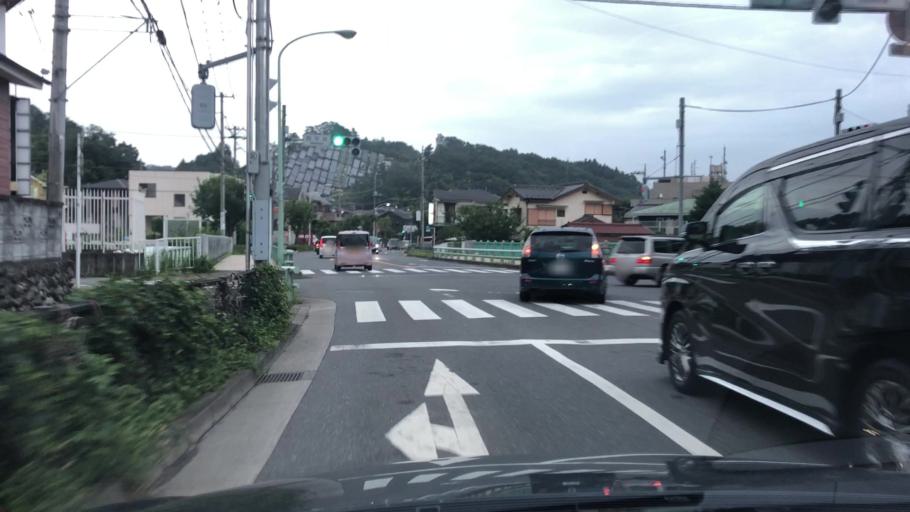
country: JP
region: Tokyo
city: Itsukaichi
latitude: 35.7424
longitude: 139.2550
